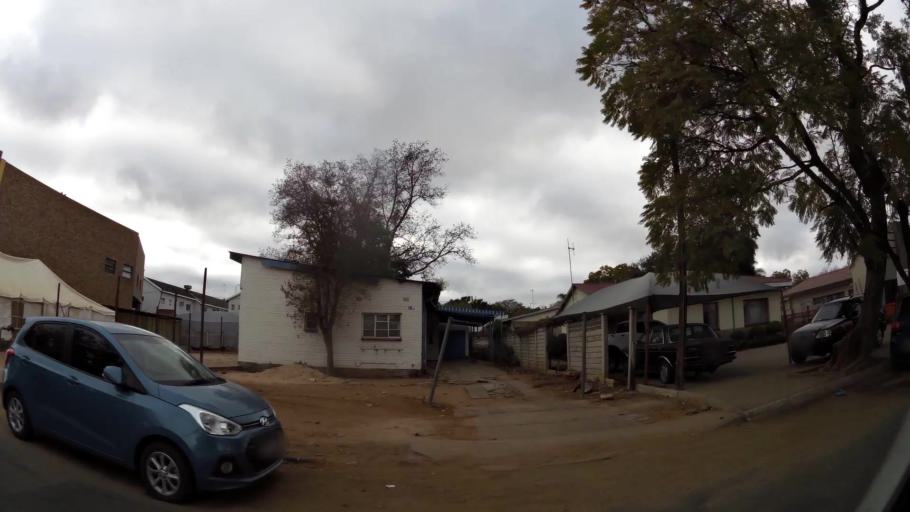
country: ZA
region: Limpopo
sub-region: Capricorn District Municipality
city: Polokwane
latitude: -23.9174
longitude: 29.4545
